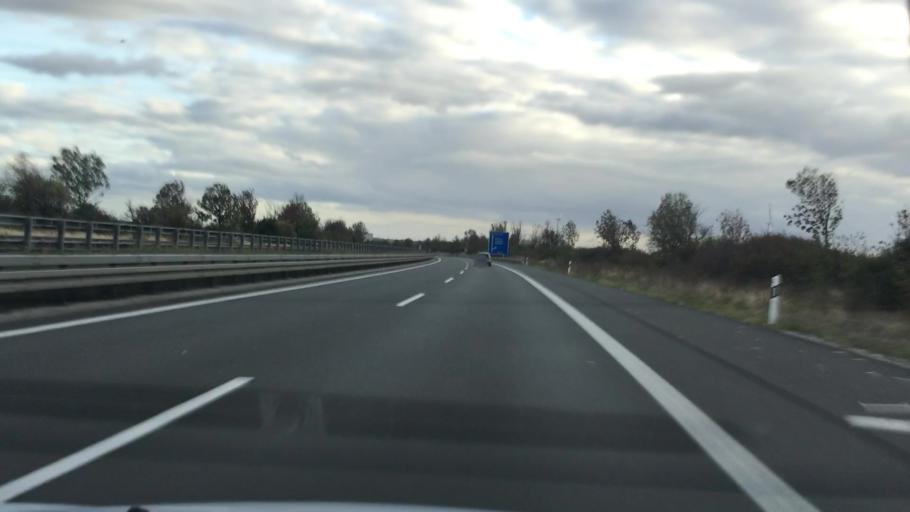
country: DE
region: Saxony-Anhalt
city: Plotzkau
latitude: 51.7437
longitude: 11.6658
